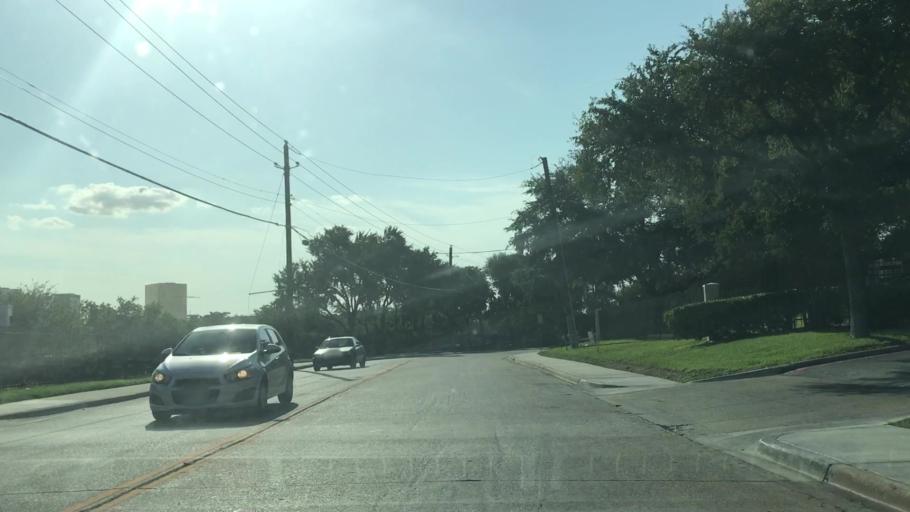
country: US
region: Texas
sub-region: Dallas County
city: University Park
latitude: 32.8649
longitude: -96.7560
